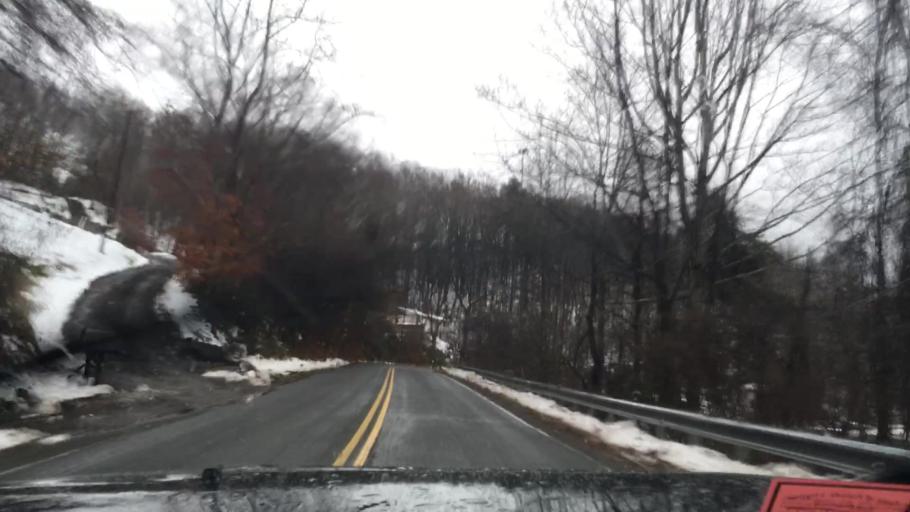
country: US
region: Virginia
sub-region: Pulaski County
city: Dublin
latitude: 37.0097
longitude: -80.6876
